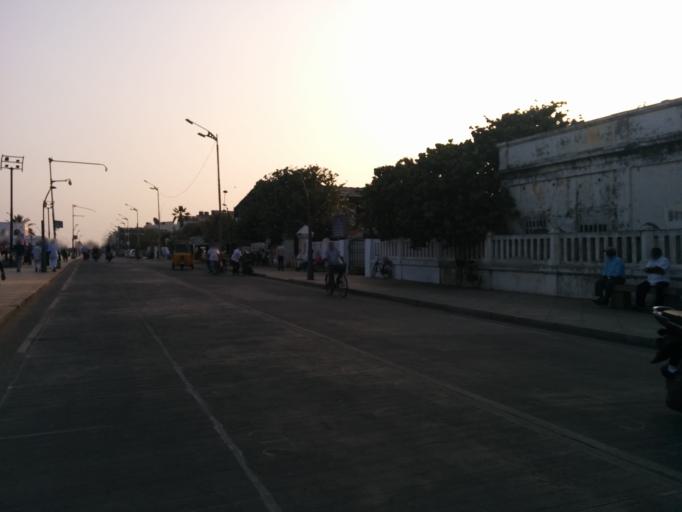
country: IN
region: Pondicherry
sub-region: Puducherry
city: Puducherry
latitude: 11.9331
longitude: 79.8360
